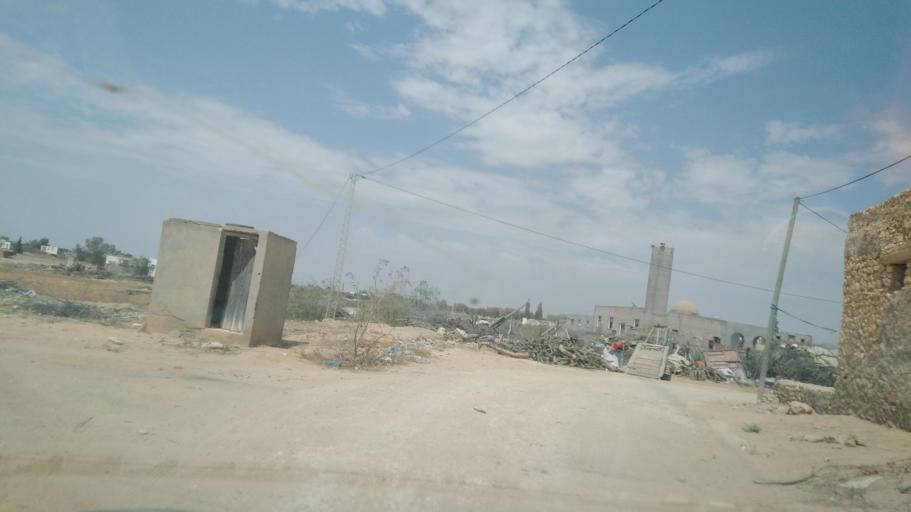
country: TN
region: Safaqis
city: Sfax
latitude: 34.7420
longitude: 10.5612
